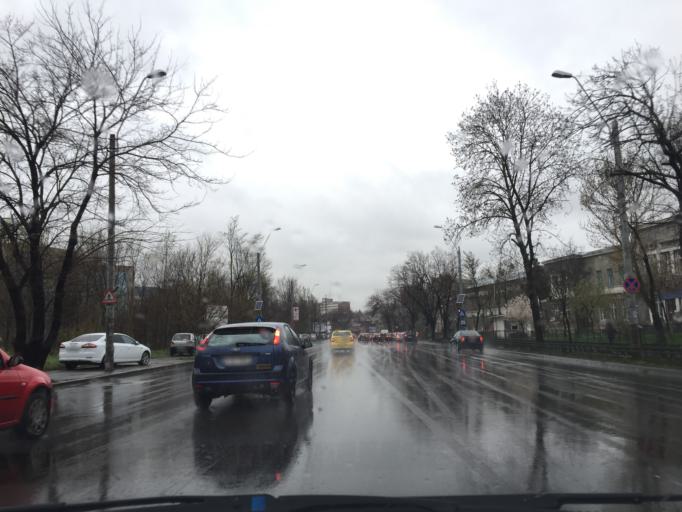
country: RO
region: Bucuresti
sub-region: Municipiul Bucuresti
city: Bucuresti
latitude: 44.4304
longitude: 26.0620
